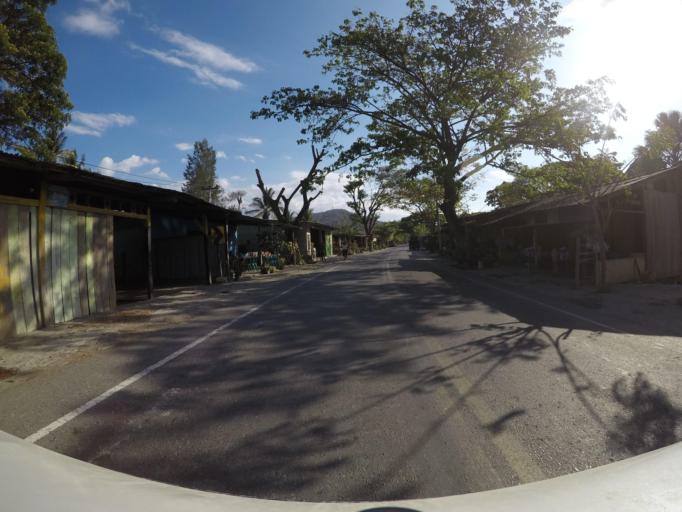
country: TL
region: Liquica
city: Maubara
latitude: -8.7379
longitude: 125.1365
